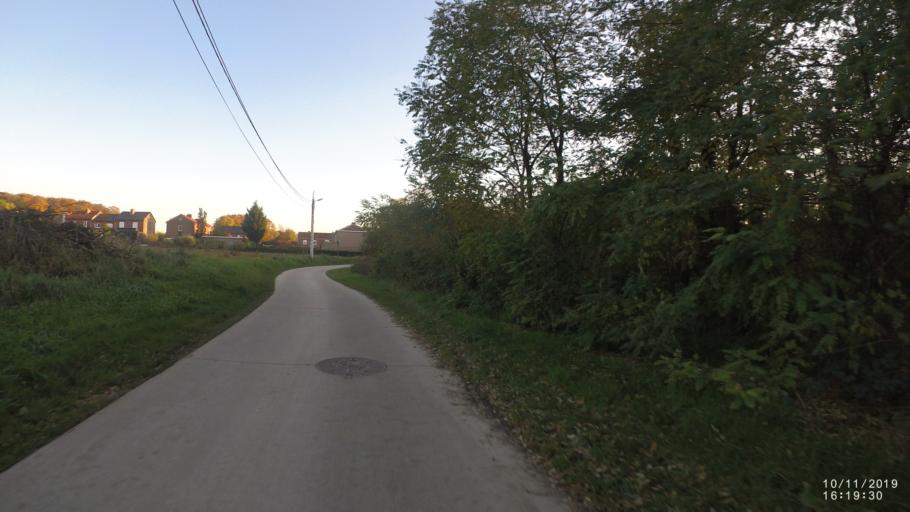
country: BE
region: Flanders
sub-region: Provincie Vlaams-Brabant
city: Lubbeek
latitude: 50.8852
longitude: 4.8504
